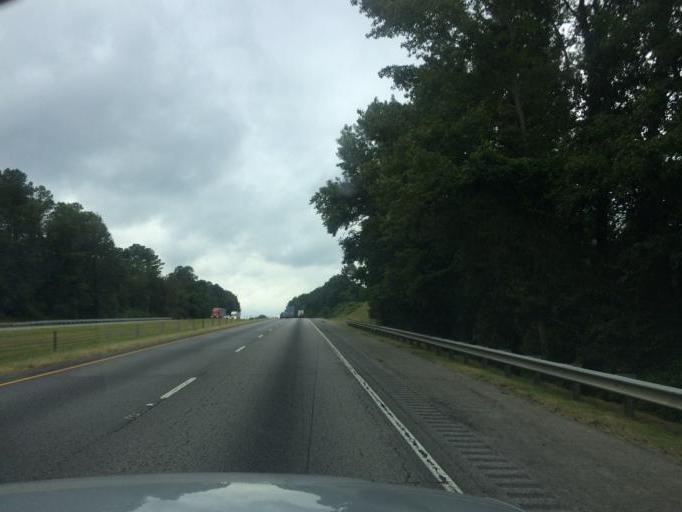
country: US
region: Georgia
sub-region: Franklin County
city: Carnesville
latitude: 34.3279
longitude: -83.3574
